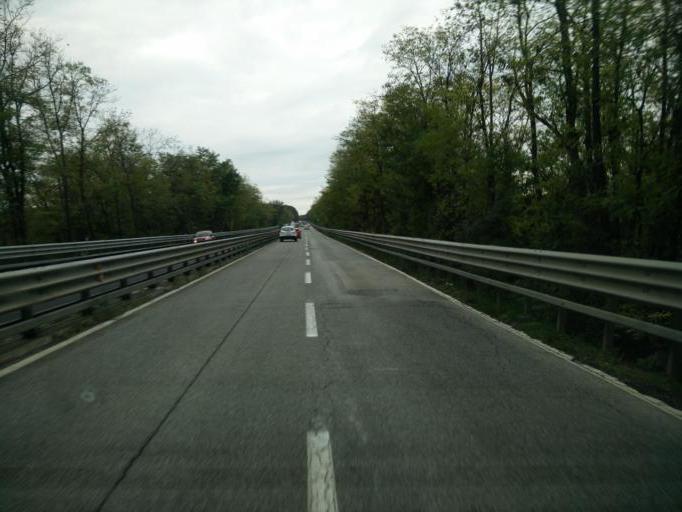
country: IT
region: Tuscany
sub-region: Provincia di Siena
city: Castellina Scalo
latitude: 43.4009
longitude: 11.1916
